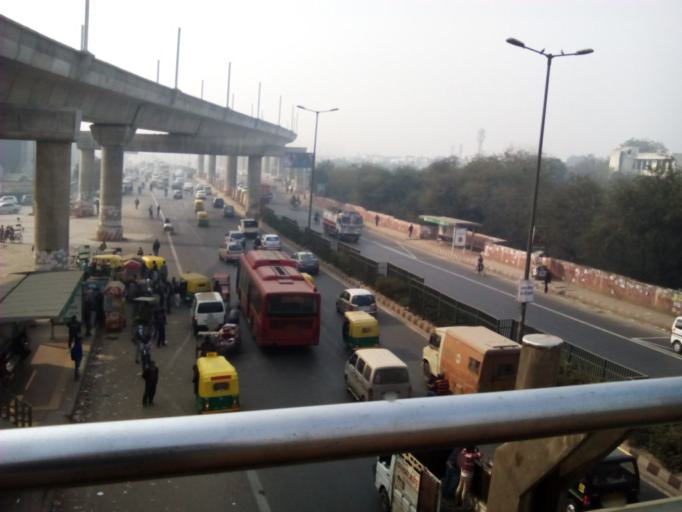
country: IN
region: Uttar Pradesh
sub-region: Gautam Buddha Nagar
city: Noida
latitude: 28.6420
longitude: 77.3162
